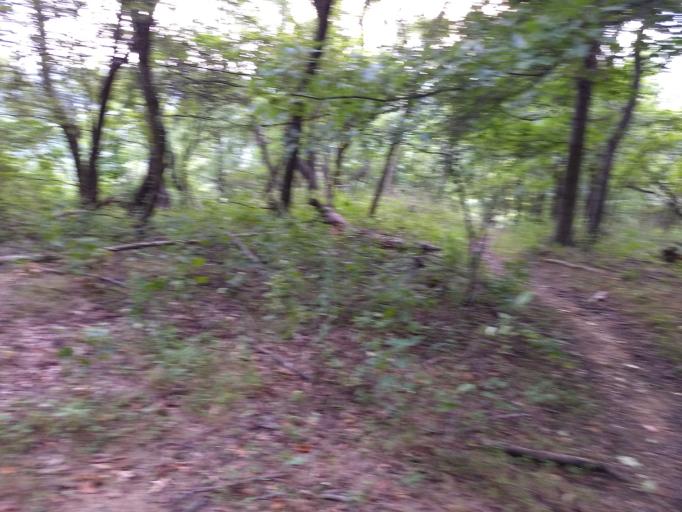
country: US
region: Pennsylvania
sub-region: Allegheny County
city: Green Tree
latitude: 40.4365
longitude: -80.0303
